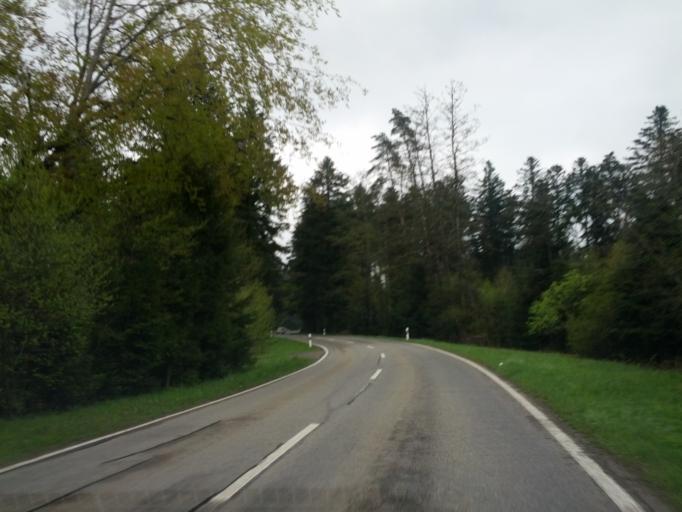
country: DE
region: Baden-Wuerttemberg
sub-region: Freiburg Region
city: Rickenbach
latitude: 47.6037
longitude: 8.0181
